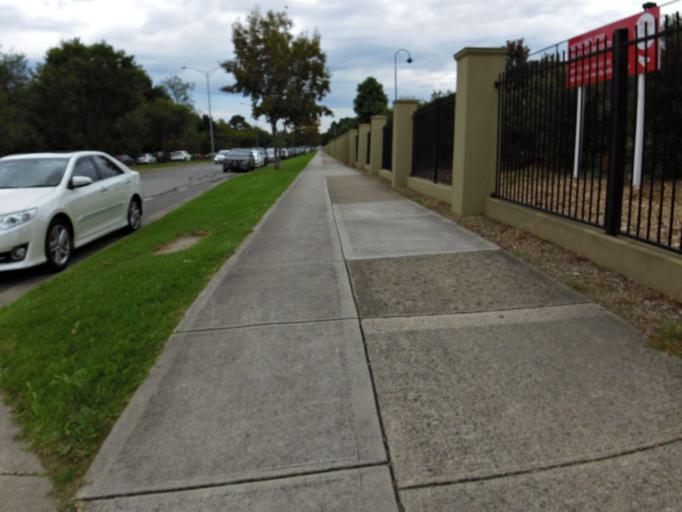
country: AU
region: Victoria
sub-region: Casey
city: Berwick
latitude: -38.0479
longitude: 145.3507
